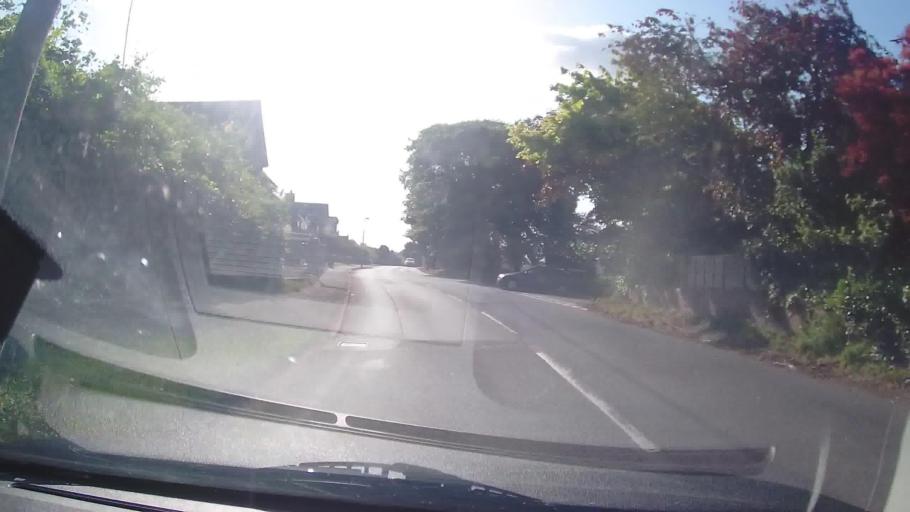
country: GB
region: England
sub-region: Shropshire
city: Withington
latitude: 52.7544
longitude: -2.6035
